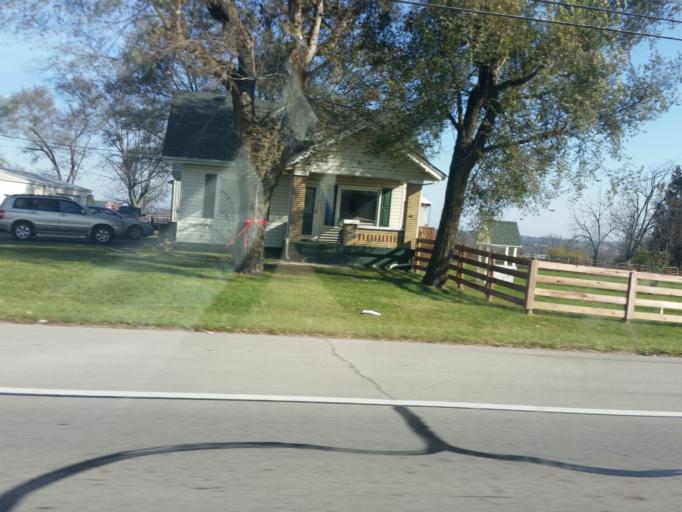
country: US
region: Ohio
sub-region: Butler County
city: Oxford
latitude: 39.4284
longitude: -84.6777
